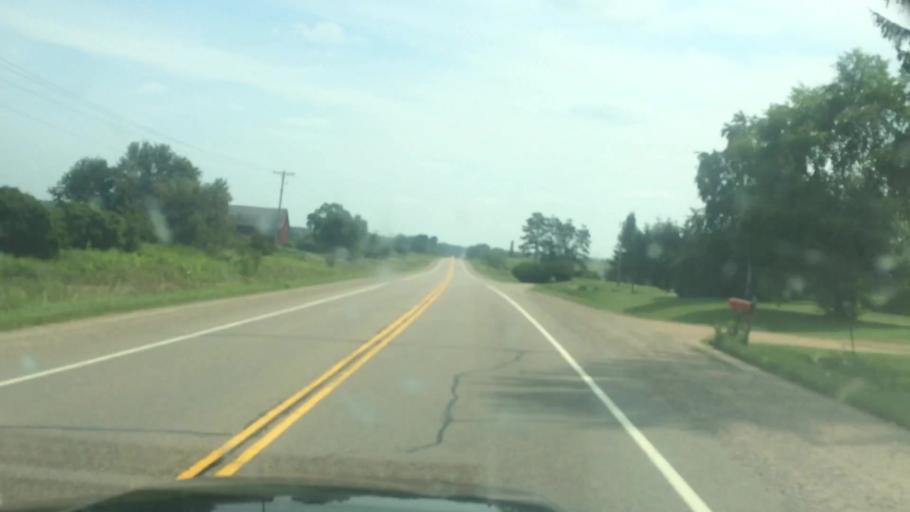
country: US
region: Wisconsin
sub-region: Langlade County
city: Antigo
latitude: 45.1686
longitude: -88.9761
